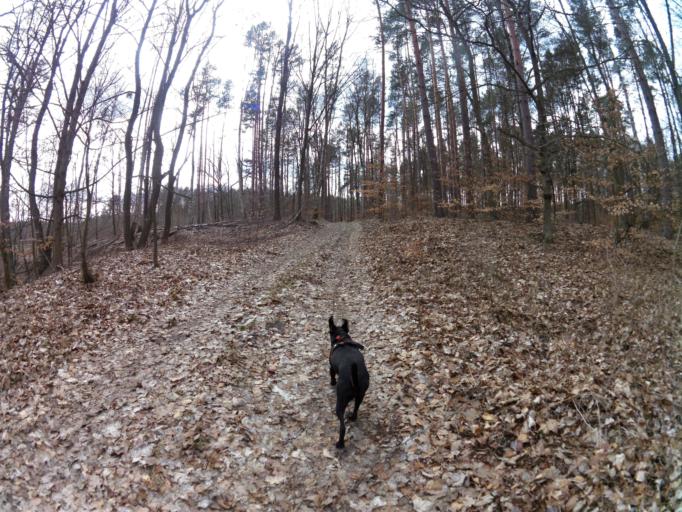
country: PL
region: Lubusz
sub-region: Powiat gorzowski
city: Lubiszyn
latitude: 52.7783
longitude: 14.8442
